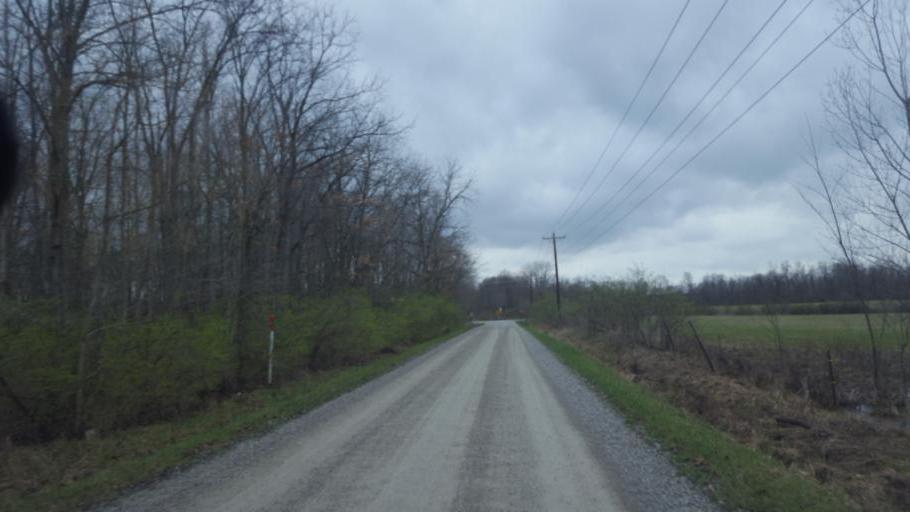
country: US
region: Ohio
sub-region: Morrow County
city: Cardington
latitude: 40.4087
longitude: -82.8500
